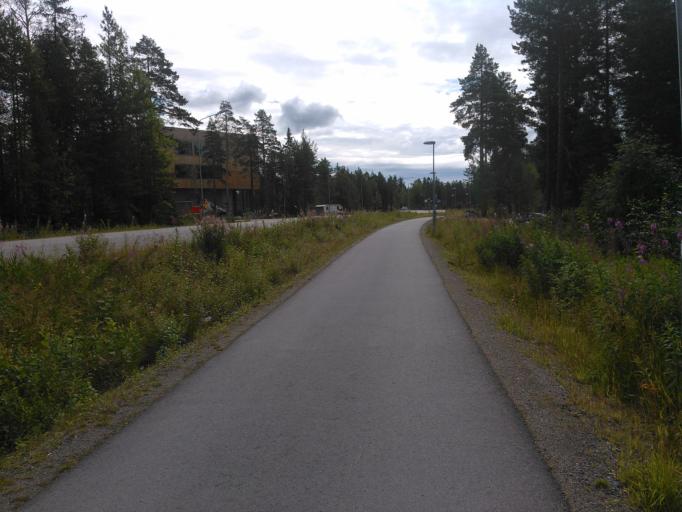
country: SE
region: Vaesterbotten
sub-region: Umea Kommun
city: Umea
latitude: 63.8225
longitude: 20.3154
